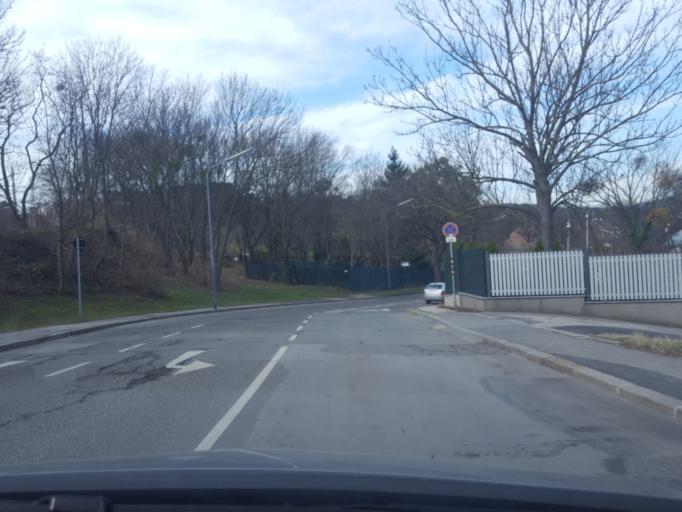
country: AT
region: Lower Austria
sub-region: Politischer Bezirk Modling
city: Perchtoldsdorf
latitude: 48.1625
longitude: 16.2911
